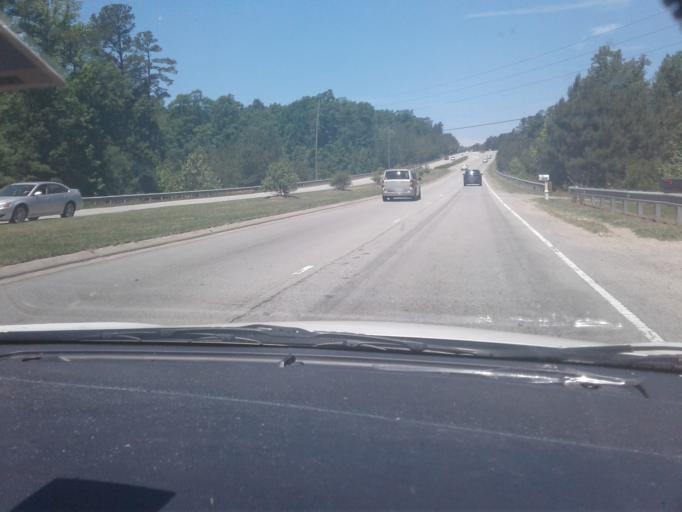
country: US
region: North Carolina
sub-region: Wake County
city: Holly Springs
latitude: 35.6205
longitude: -78.8166
